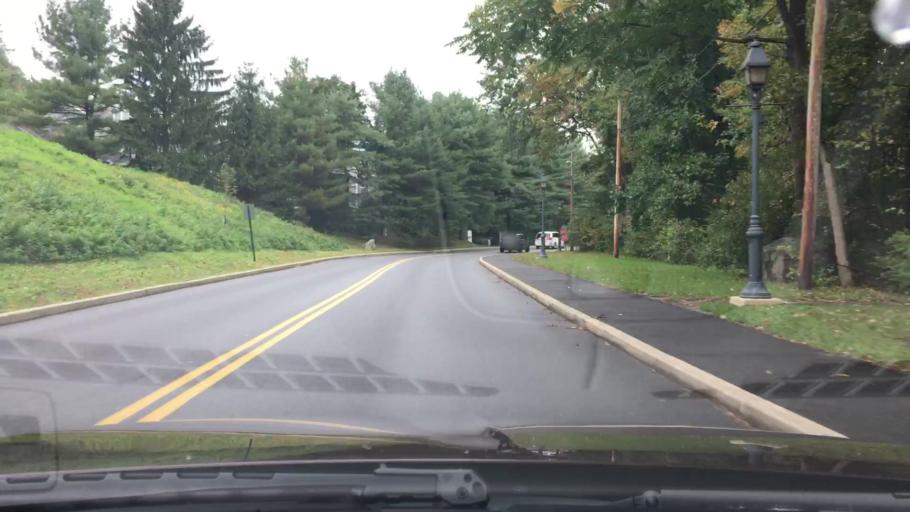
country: US
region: Connecticut
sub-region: Fairfield County
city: Wilton
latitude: 41.1843
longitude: -73.4289
